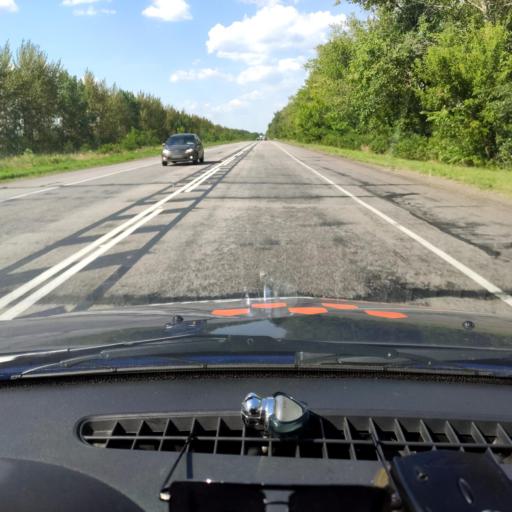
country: RU
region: Voronezj
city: Maslovka
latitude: 51.4524
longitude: 39.3038
